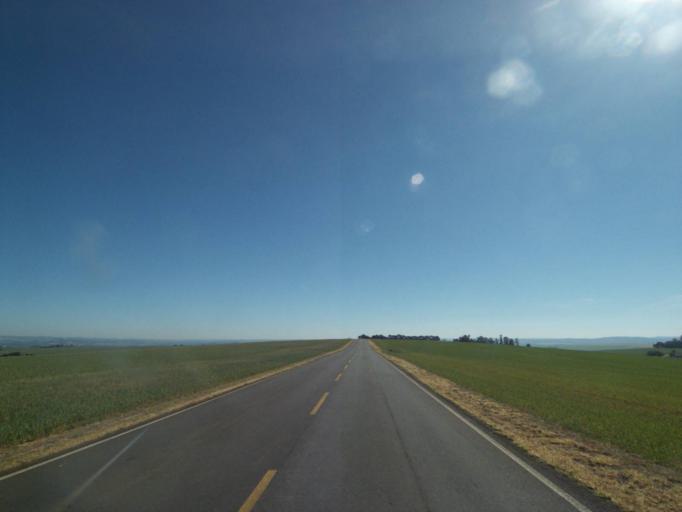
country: BR
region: Parana
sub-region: Tibagi
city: Tibagi
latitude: -24.5280
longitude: -50.3219
